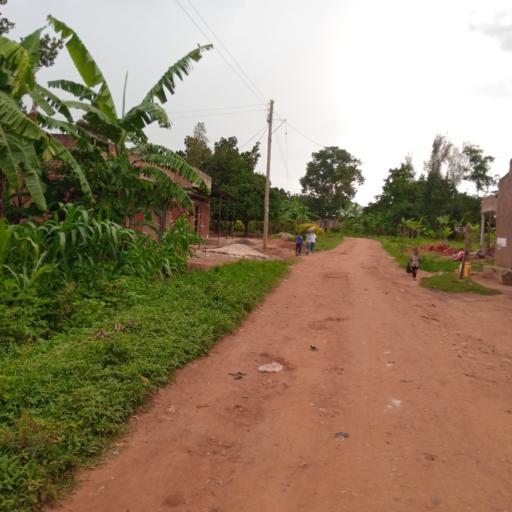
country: UG
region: Eastern Region
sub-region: Mbale District
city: Mbale
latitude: 1.1245
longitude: 34.1724
